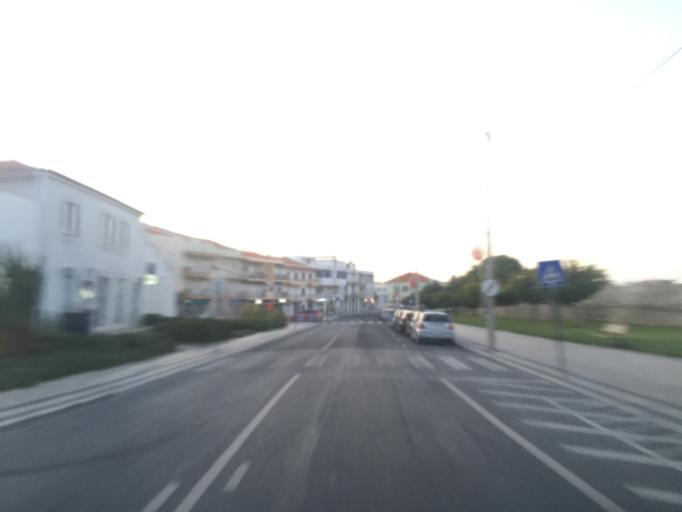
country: PT
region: Leiria
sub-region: Peniche
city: Peniche
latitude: 39.3616
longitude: -9.3789
